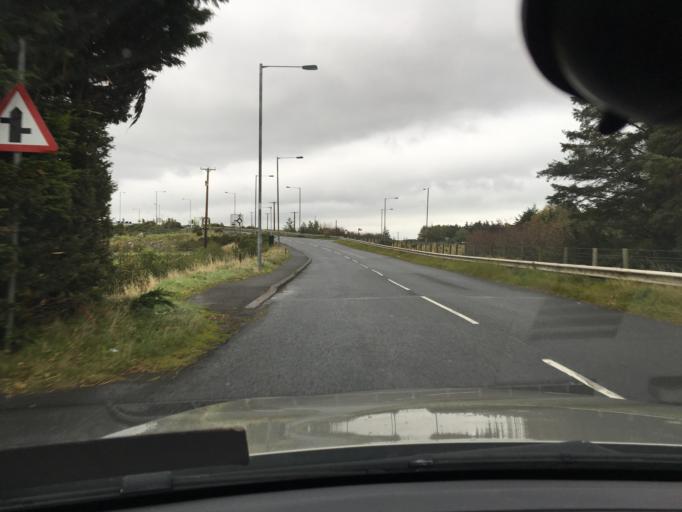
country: GB
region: Northern Ireland
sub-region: Newry and Mourne District
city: Newry
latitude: 54.1361
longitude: -6.3426
